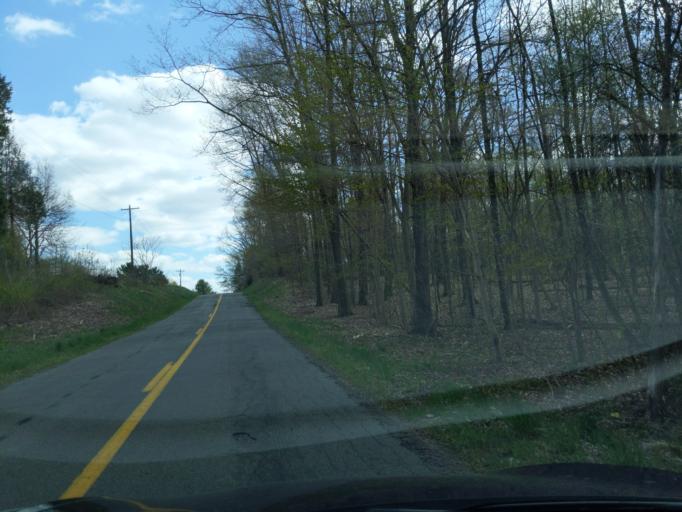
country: US
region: Michigan
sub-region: Ingham County
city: Leslie
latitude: 42.4300
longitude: -84.5409
